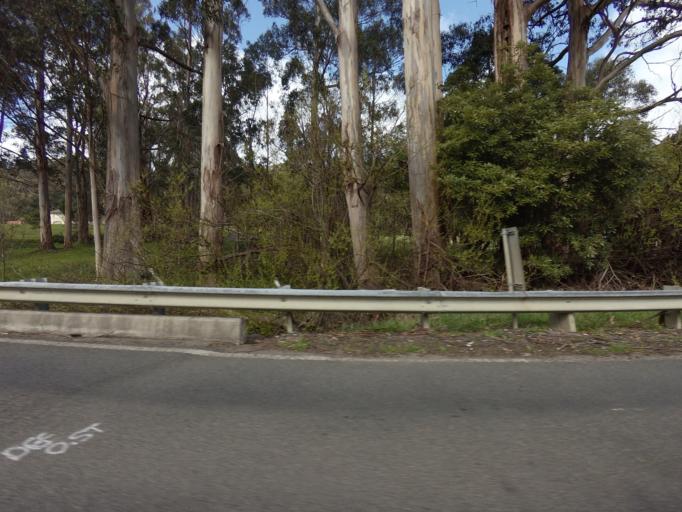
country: AU
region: Tasmania
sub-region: Huon Valley
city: Cygnet
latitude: -43.2976
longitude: 147.0102
